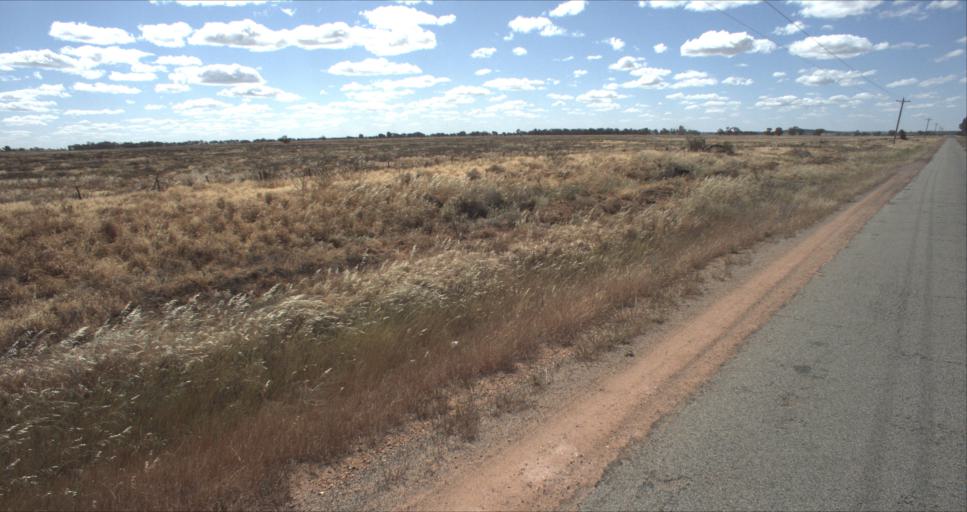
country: AU
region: New South Wales
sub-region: Leeton
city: Leeton
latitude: -34.4787
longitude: 146.2495
